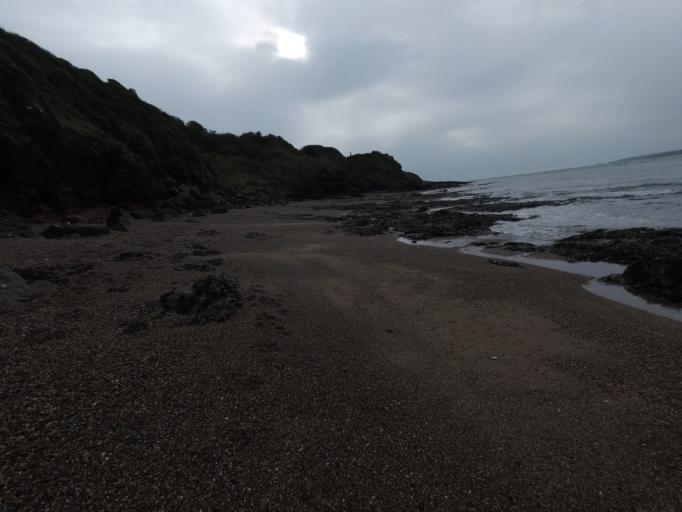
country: IE
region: Munster
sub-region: Waterford
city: Tra Mhor
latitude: 52.1385
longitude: -7.0993
